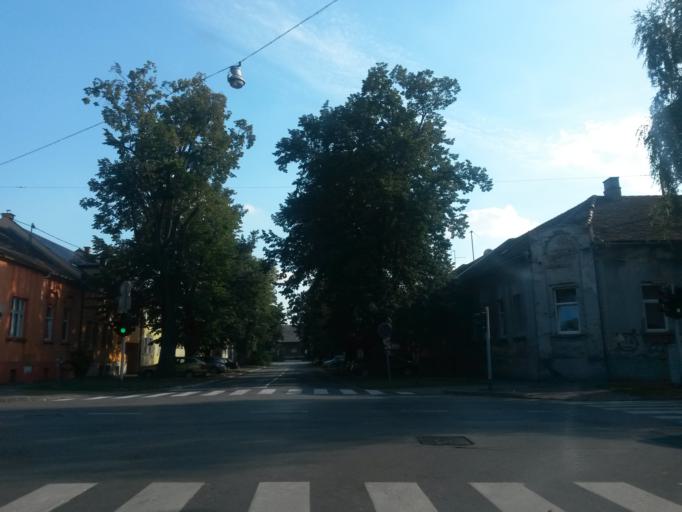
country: HR
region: Osjecko-Baranjska
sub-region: Grad Osijek
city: Osijek
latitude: 45.5549
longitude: 18.6862
